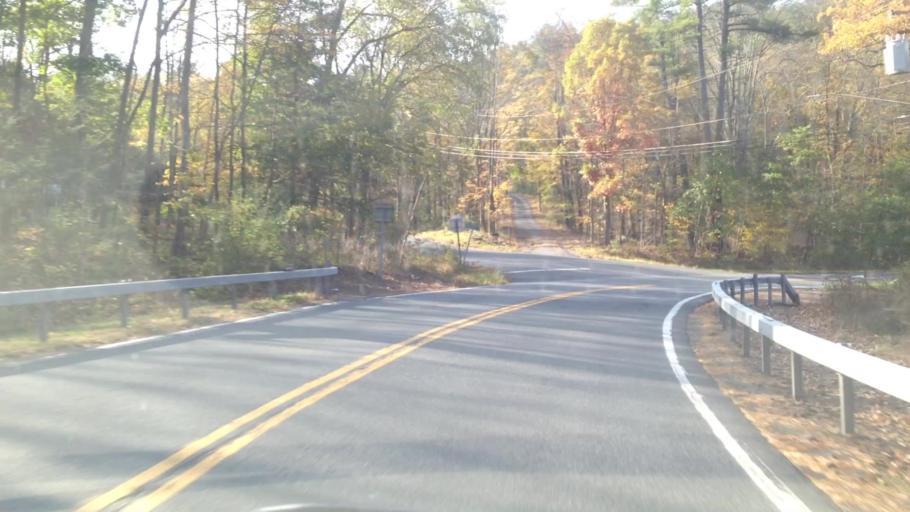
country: US
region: New York
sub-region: Ulster County
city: Tillson
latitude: 41.8213
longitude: -74.0456
